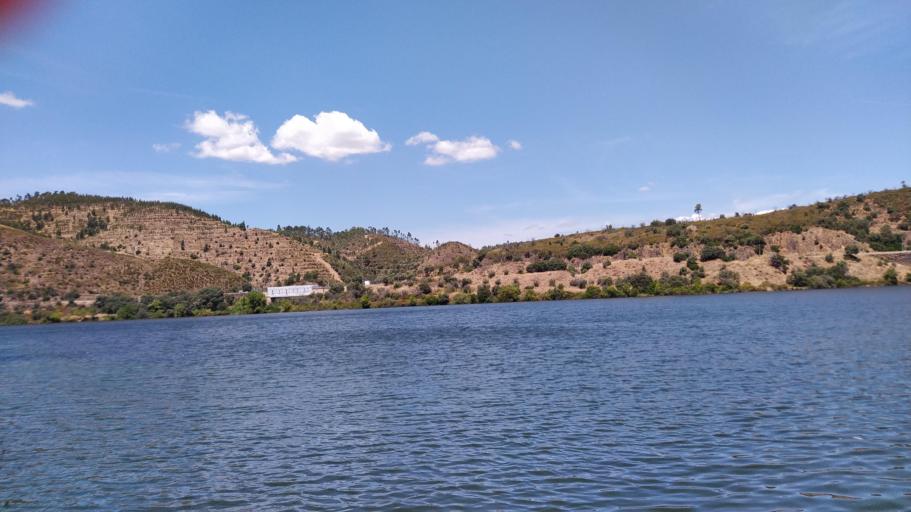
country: PT
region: Portalegre
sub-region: Nisa
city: Nisa
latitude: 39.6361
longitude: -7.6987
